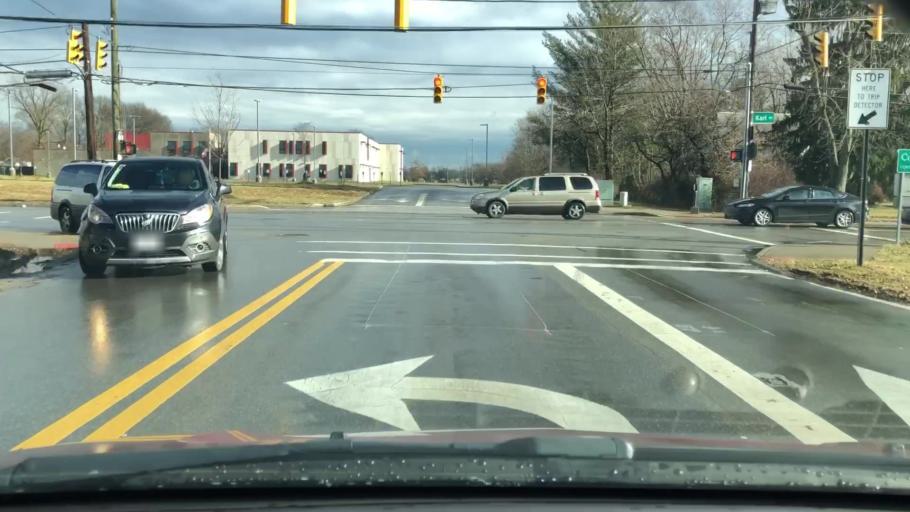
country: US
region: Ohio
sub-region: Franklin County
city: Minerva Park
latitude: 40.0472
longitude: -82.9773
